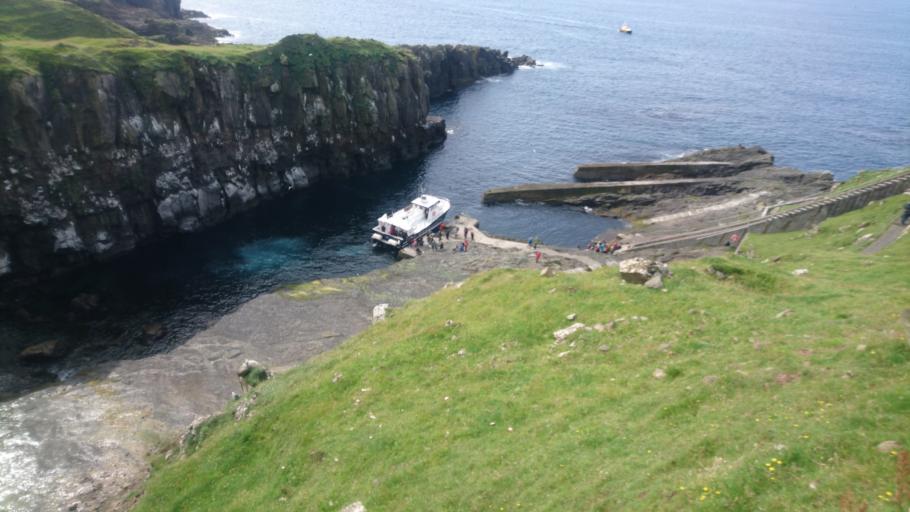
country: FO
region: Vagar
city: Sorvagur
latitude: 62.1027
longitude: -7.6479
